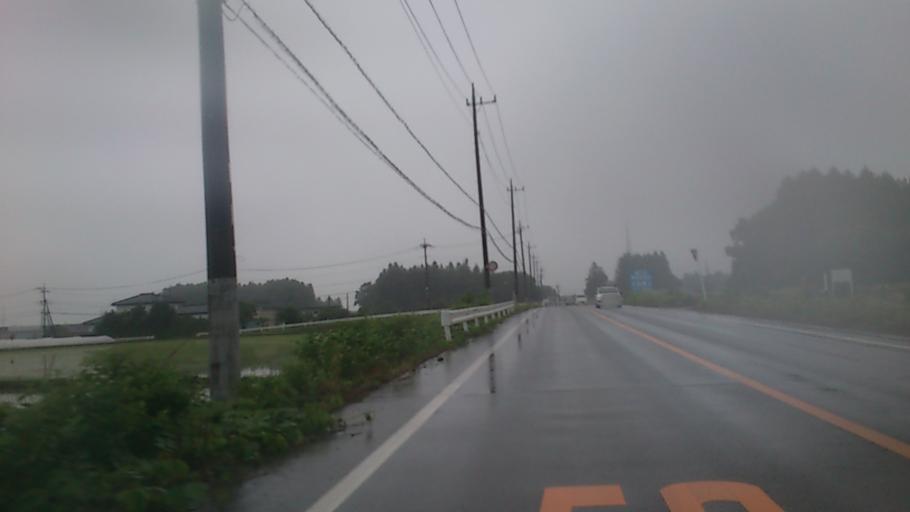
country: JP
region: Tochigi
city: Otawara
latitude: 36.9056
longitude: 139.9939
